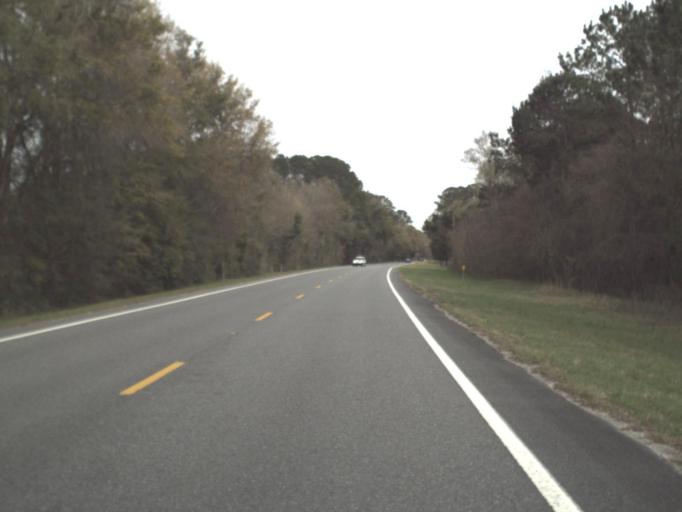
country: US
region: Florida
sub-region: Leon County
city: Woodville
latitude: 30.2382
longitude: -84.2629
